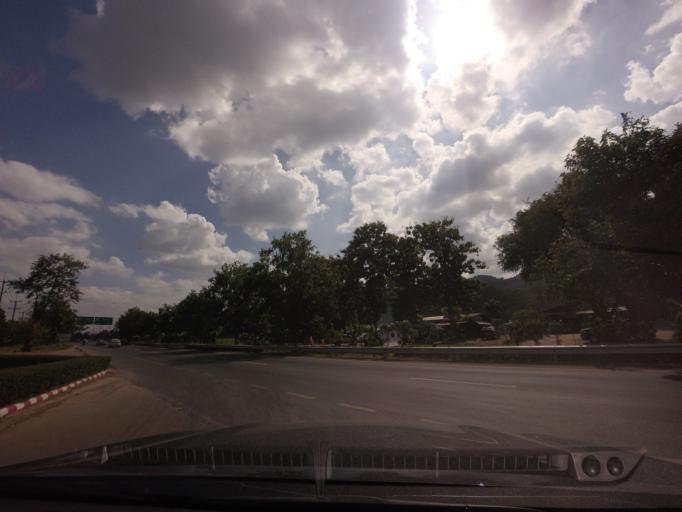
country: TH
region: Phetchabun
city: Wichian Buri
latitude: 15.6556
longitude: 101.0396
